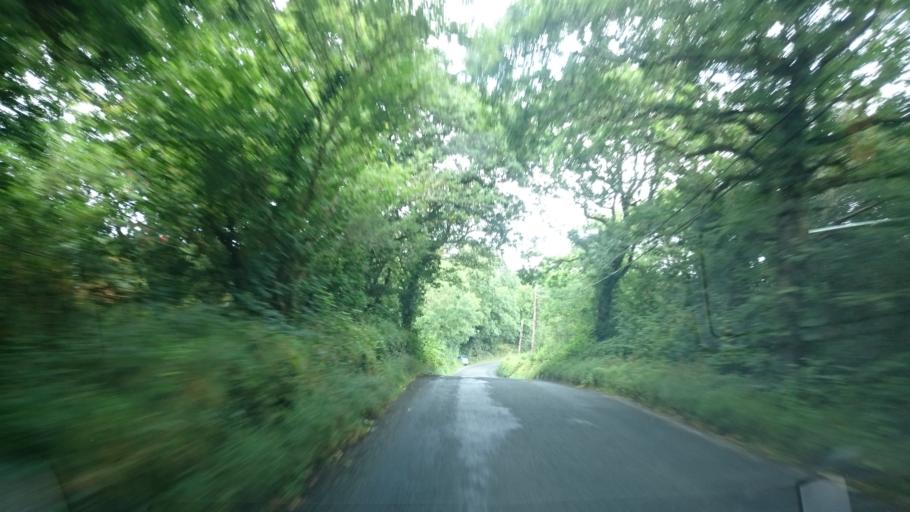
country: IE
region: Connaught
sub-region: Maigh Eo
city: Westport
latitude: 53.9034
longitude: -9.5502
